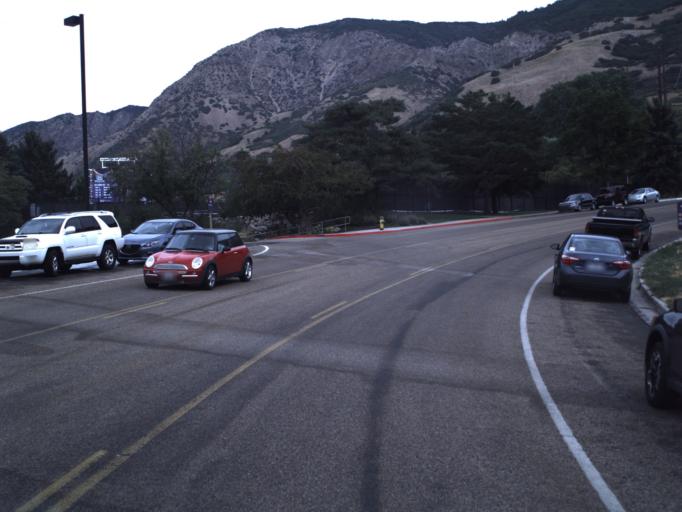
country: US
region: Utah
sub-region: Weber County
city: South Ogden
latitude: 41.1895
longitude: -111.9423
